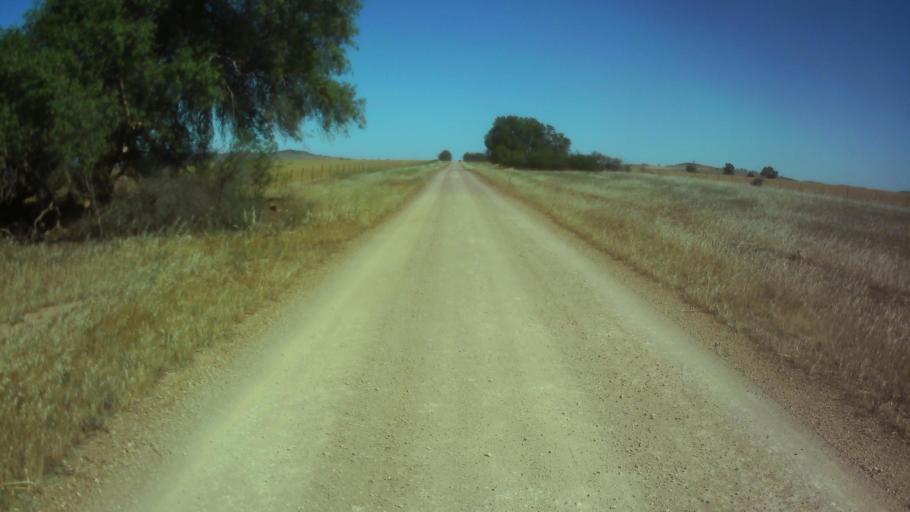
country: AU
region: New South Wales
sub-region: Weddin
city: Grenfell
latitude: -33.9878
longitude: 148.3359
